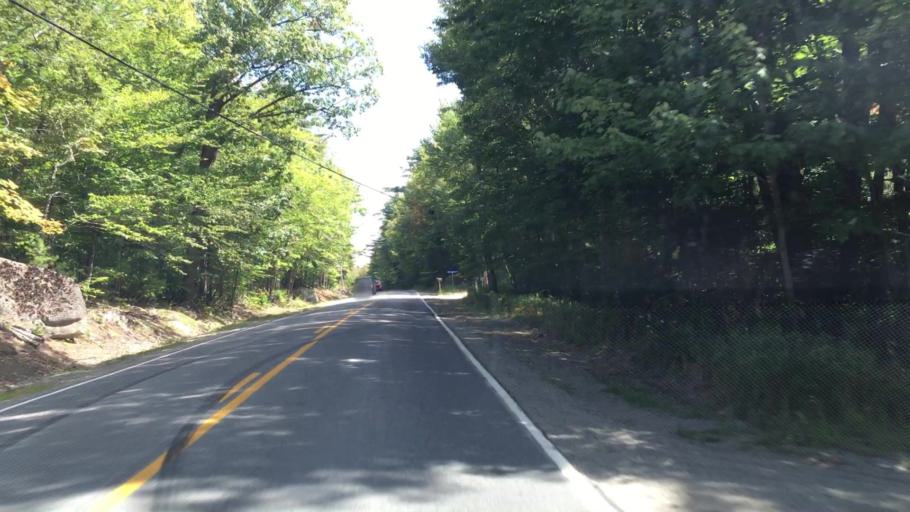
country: US
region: Maine
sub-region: Penobscot County
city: Holden
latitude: 44.7939
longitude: -68.5191
